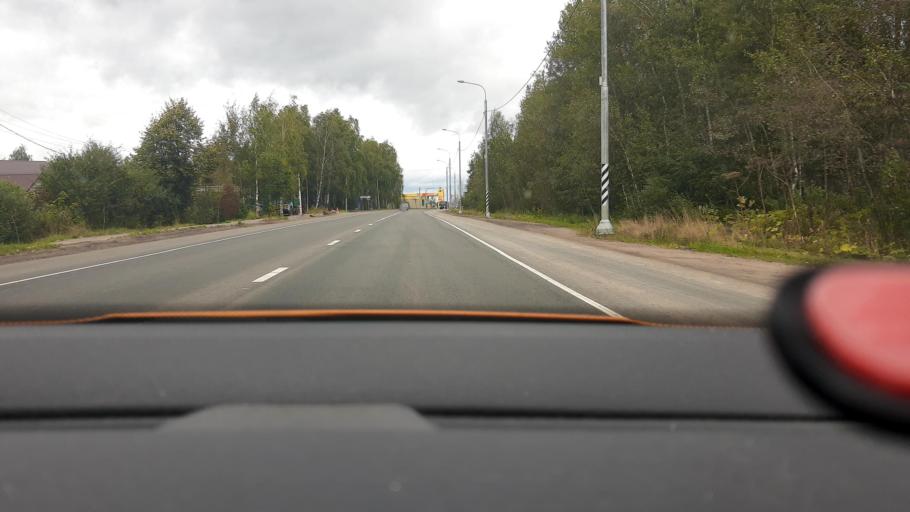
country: RU
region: Moskovskaya
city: Krasnoarmeysk
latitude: 56.0743
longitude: 38.0381
